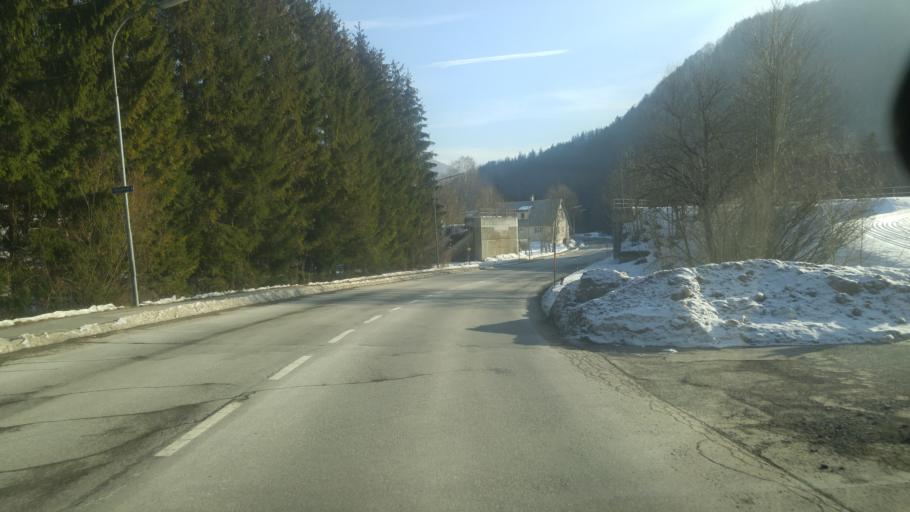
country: AT
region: Lower Austria
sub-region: Politischer Bezirk Lilienfeld
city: Lilienfeld
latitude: 47.9755
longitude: 15.5693
